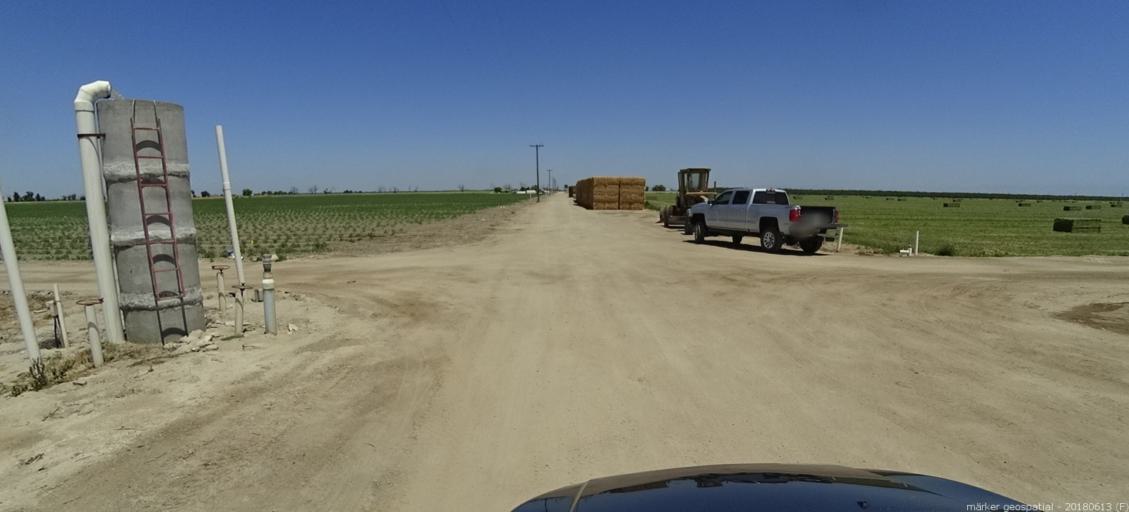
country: US
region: California
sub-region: Madera County
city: Chowchilla
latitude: 36.9892
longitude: -120.3465
